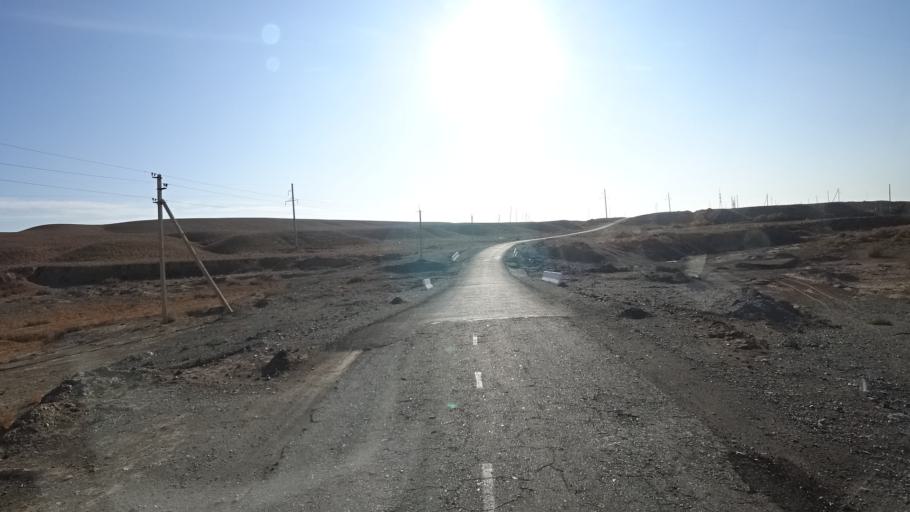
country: UZ
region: Navoiy
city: Beshrabot
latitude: 40.2346
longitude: 65.4214
